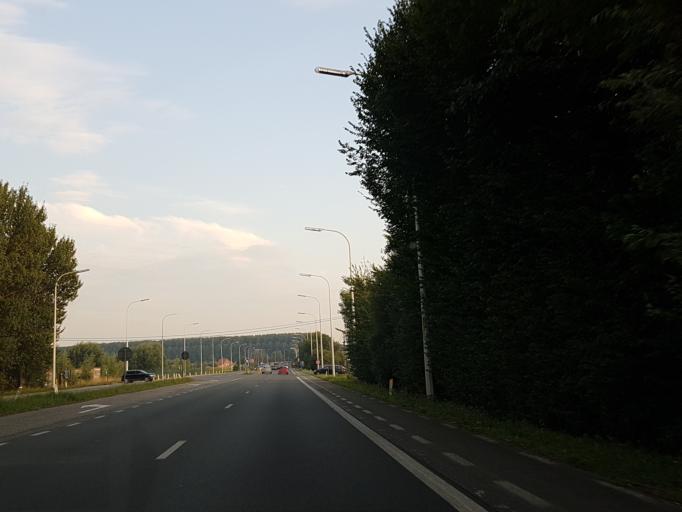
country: NL
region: Zeeland
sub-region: Gemeente Sluis
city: Sluis
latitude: 51.2506
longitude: 3.3948
